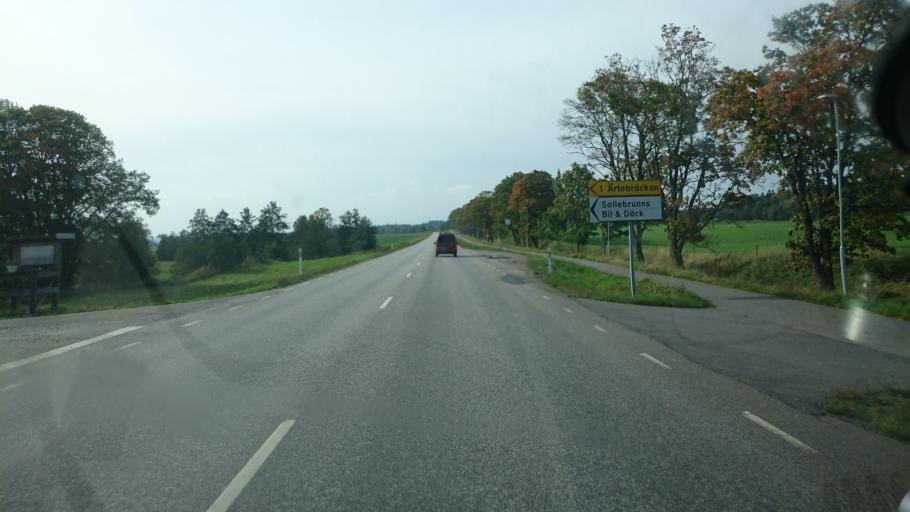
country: SE
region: Vaestra Goetaland
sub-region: Alingsas Kommun
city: Sollebrunn
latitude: 58.0975
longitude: 12.5060
